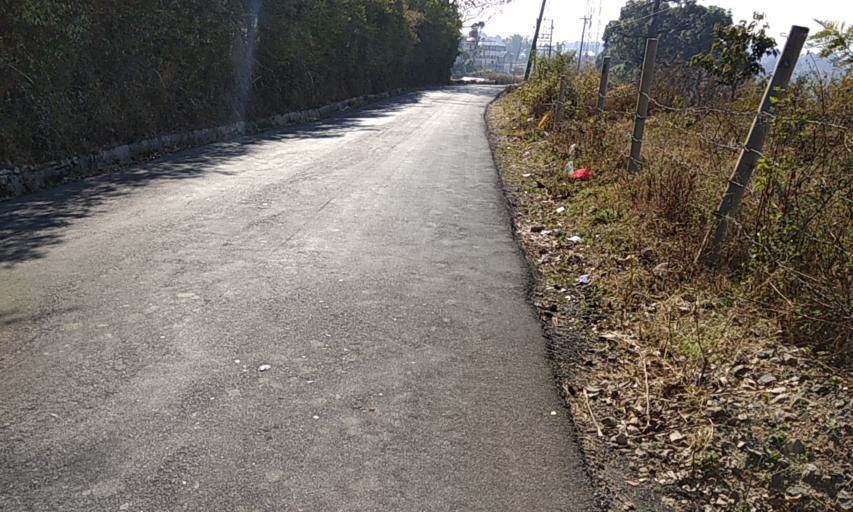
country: IN
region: Himachal Pradesh
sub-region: Kangra
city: Palampur
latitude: 32.1200
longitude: 76.5255
